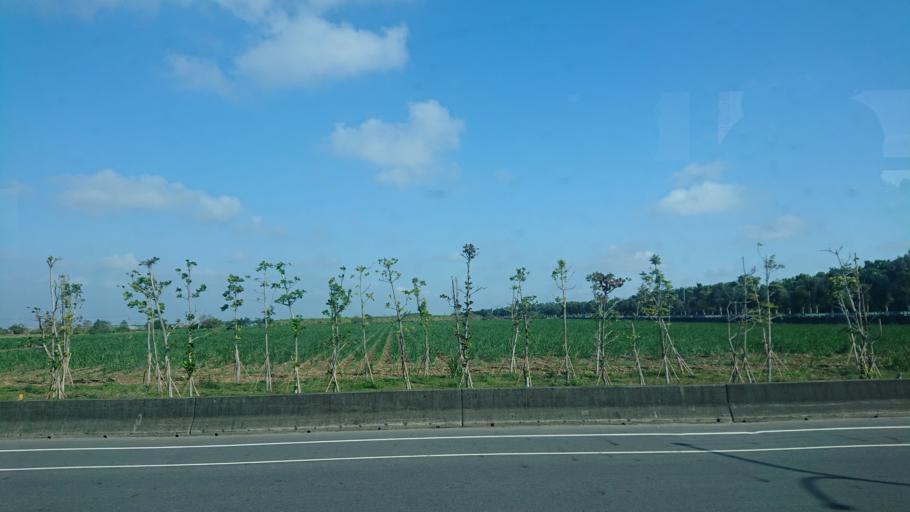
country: TW
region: Taiwan
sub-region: Chiayi
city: Taibao
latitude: 23.4565
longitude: 120.3165
